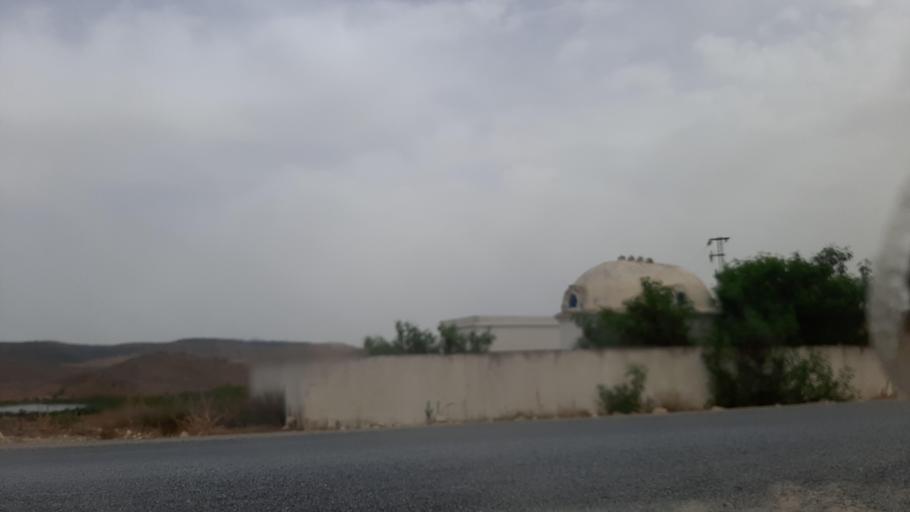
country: TN
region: Tunis
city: La Mohammedia
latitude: 36.5654
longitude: 10.1501
